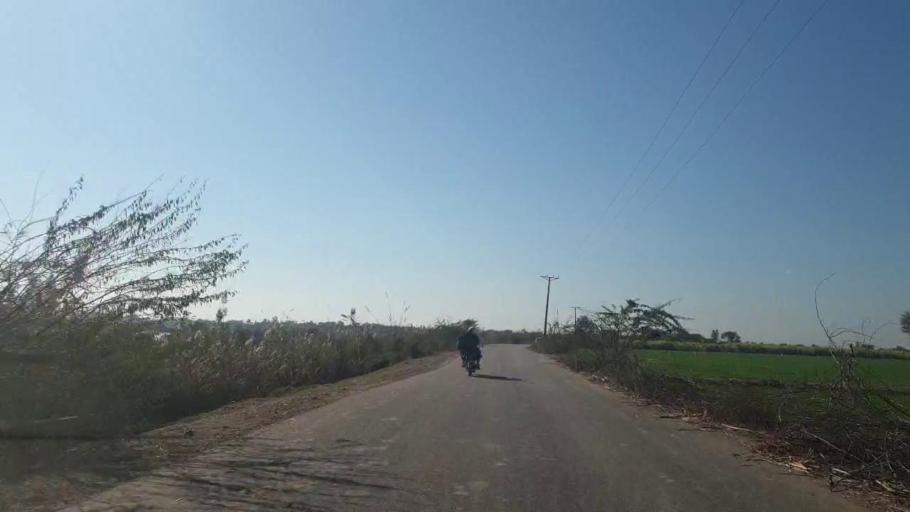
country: PK
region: Sindh
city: Kot Diji
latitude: 27.3024
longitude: 68.6440
